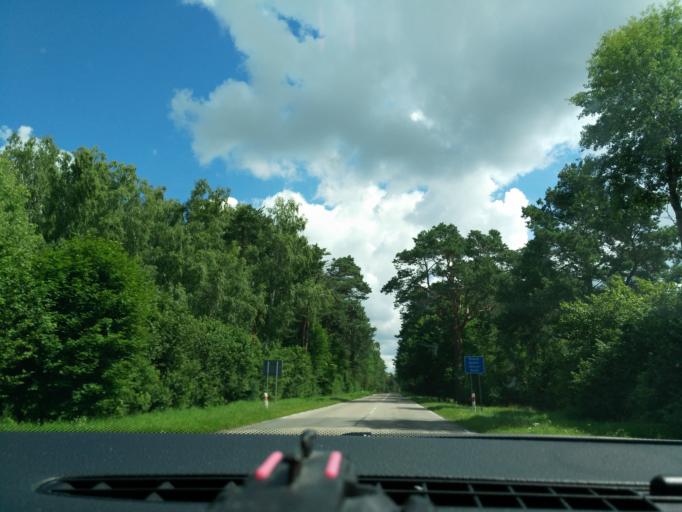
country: PL
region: Podlasie
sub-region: Powiat siemiatycki
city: Dziadkowice
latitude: 52.5902
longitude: 22.9461
